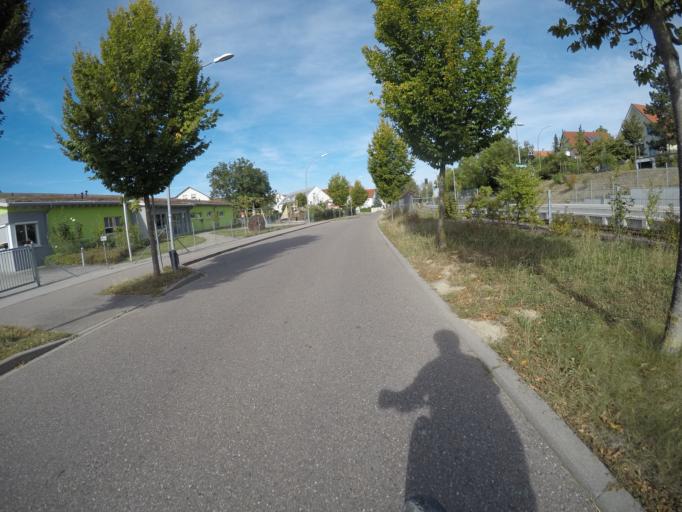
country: DE
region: Baden-Wuerttemberg
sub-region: Regierungsbezirk Stuttgart
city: Schwieberdingen
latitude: 48.8556
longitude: 9.0949
